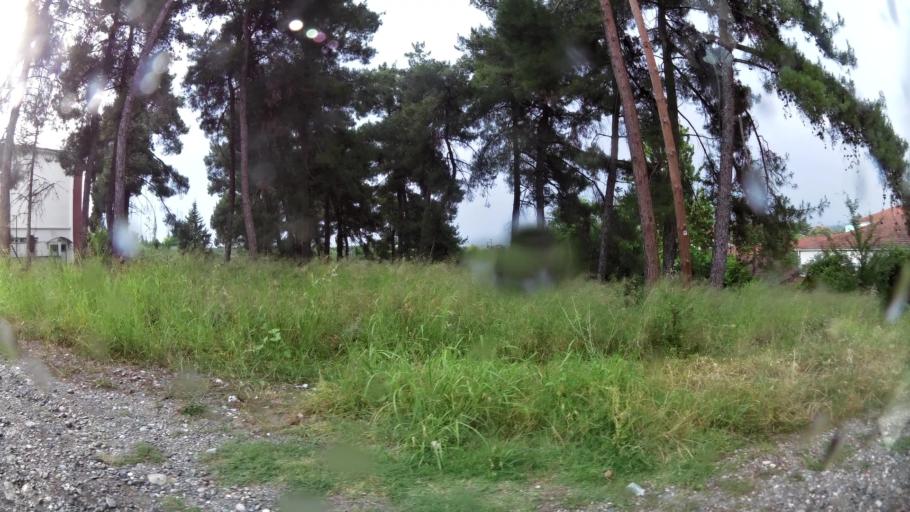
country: GR
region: Central Macedonia
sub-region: Nomos Imathias
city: Veroia
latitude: 40.5414
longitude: 22.1981
